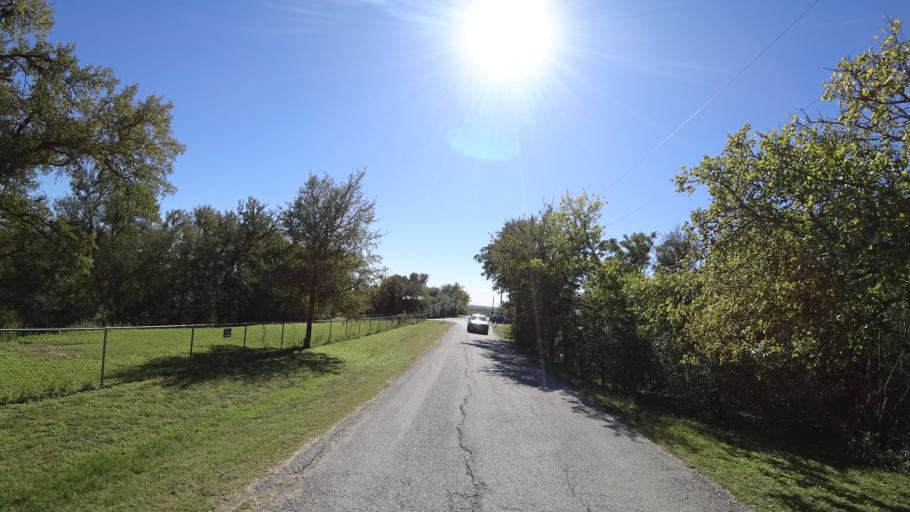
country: US
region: Texas
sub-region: Travis County
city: Hornsby Bend
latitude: 30.2812
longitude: -97.6425
